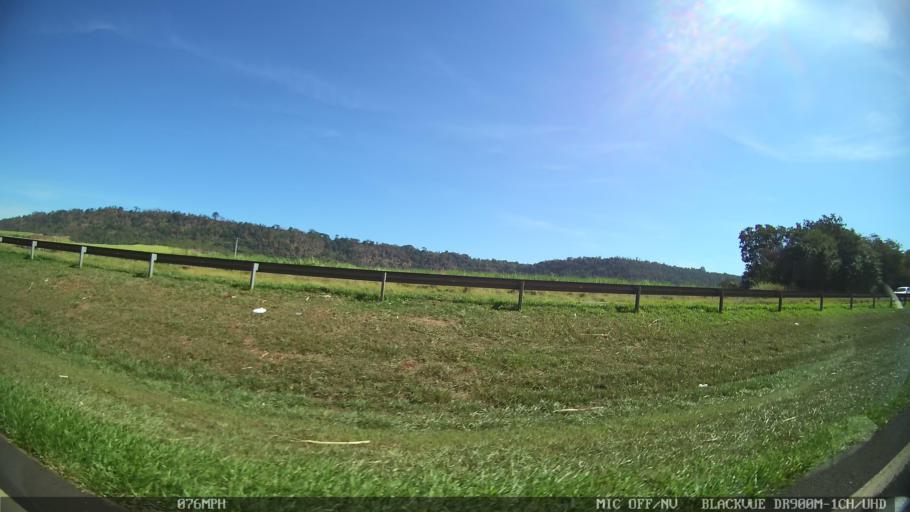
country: BR
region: Sao Paulo
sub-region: Sao Simao
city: Sao Simao
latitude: -21.5094
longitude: -47.6424
